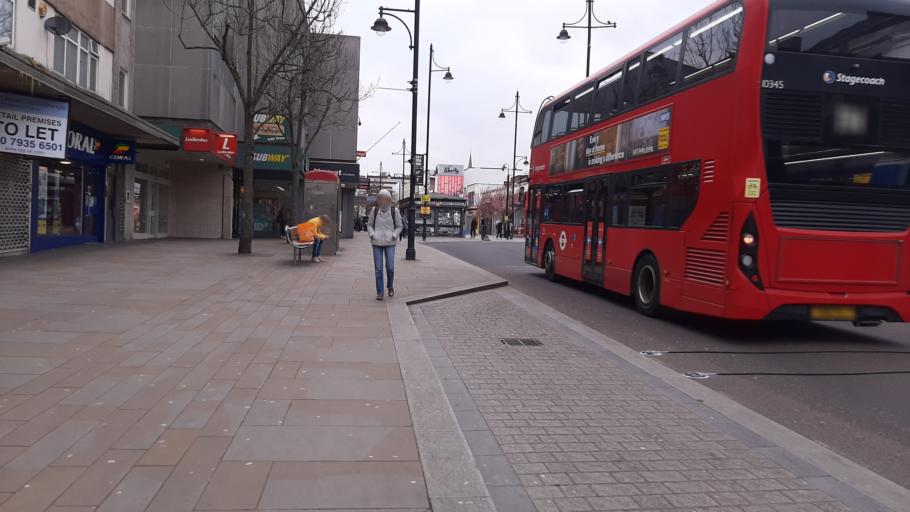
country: GB
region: England
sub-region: Greater London
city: Romford
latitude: 51.5760
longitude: 0.1826
